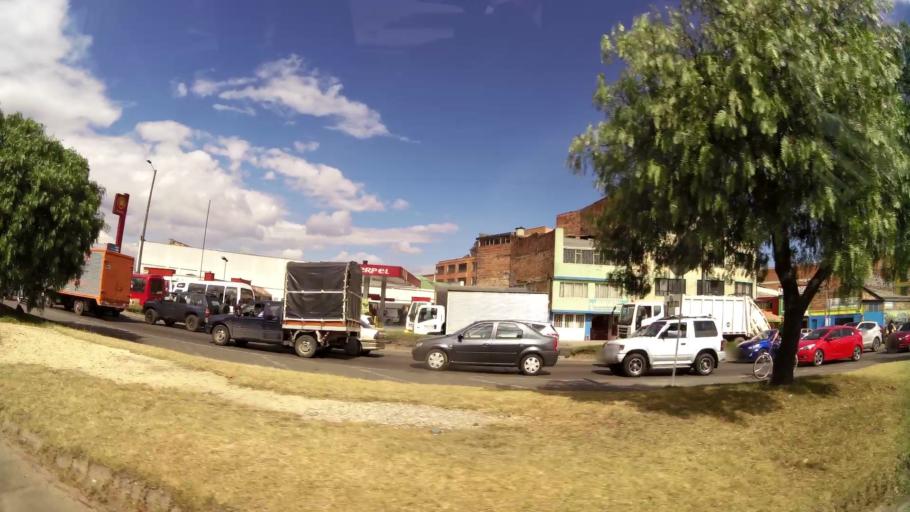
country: CO
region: Bogota D.C.
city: Bogota
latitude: 4.6106
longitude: -74.1410
